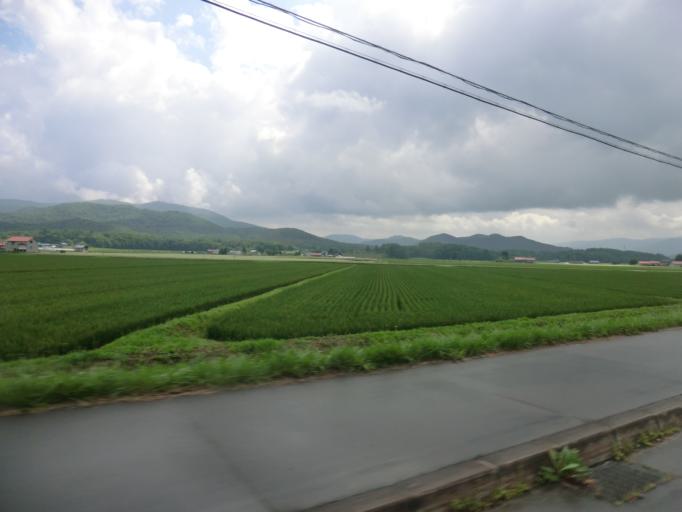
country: JP
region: Hokkaido
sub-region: Asahikawa-shi
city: Asahikawa
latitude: 44.0241
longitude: 142.1524
